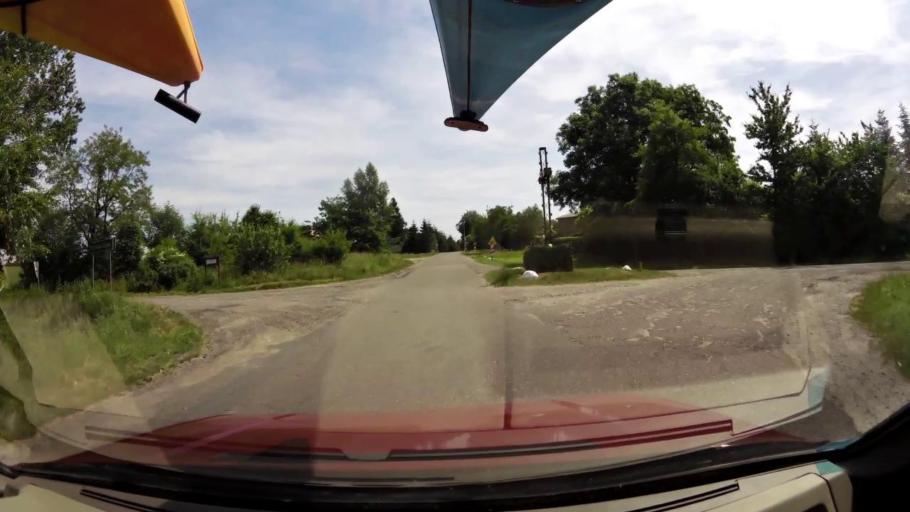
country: PL
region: West Pomeranian Voivodeship
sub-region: Powiat slawienski
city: Darlowo
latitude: 54.3196
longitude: 16.4071
